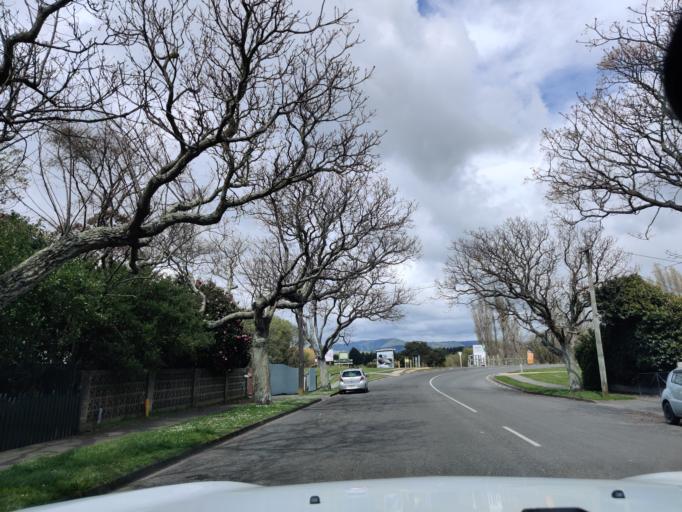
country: NZ
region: Manawatu-Wanganui
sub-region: Palmerston North City
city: Palmerston North
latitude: -40.3817
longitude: 175.5865
